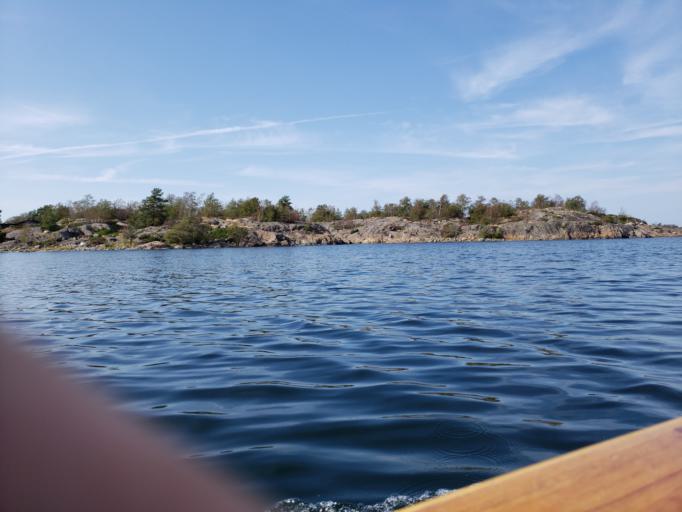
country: FI
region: Varsinais-Suomi
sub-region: Aboland-Turunmaa
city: Dragsfjaerd
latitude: 59.8510
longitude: 22.2128
